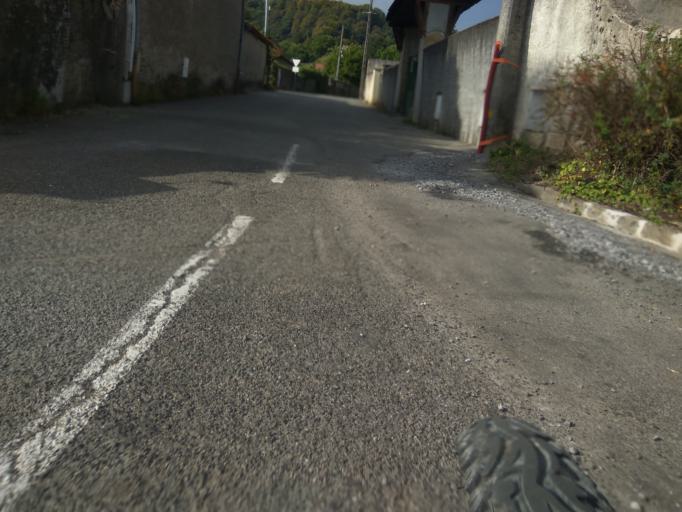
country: FR
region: Aquitaine
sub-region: Departement des Pyrenees-Atlantiques
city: Bizanos
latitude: 43.2759
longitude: -0.3507
